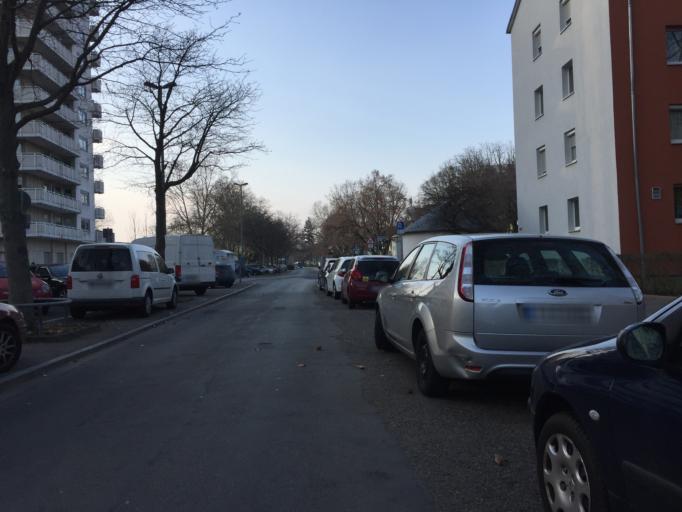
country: DE
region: Hesse
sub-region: Regierungsbezirk Darmstadt
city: Frankfurt am Main
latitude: 50.1372
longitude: 8.6648
